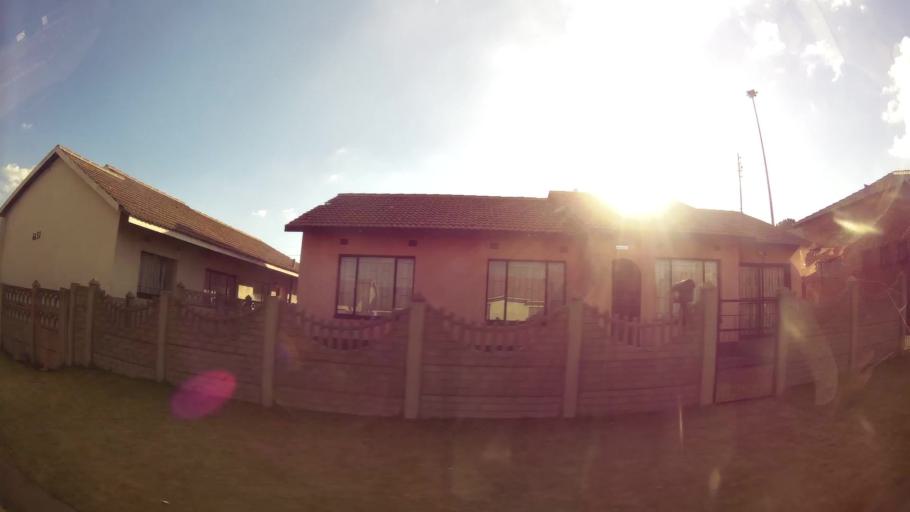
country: ZA
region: Mpumalanga
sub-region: Nkangala District Municipality
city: Witbank
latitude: -25.8698
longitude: 29.1819
